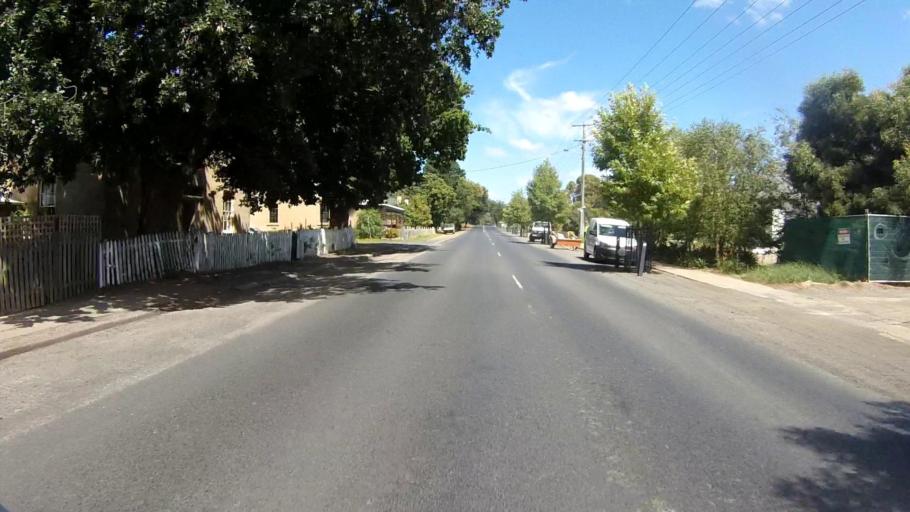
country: AU
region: Tasmania
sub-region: Clarence
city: Cambridge
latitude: -42.7373
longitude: 147.4337
